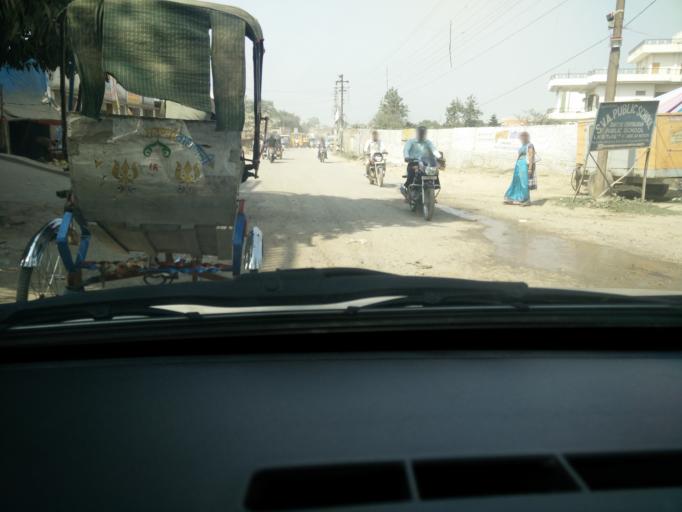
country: IN
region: Uttar Pradesh
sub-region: Varanasi
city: Ramnagar
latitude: 25.2680
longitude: 83.0159
